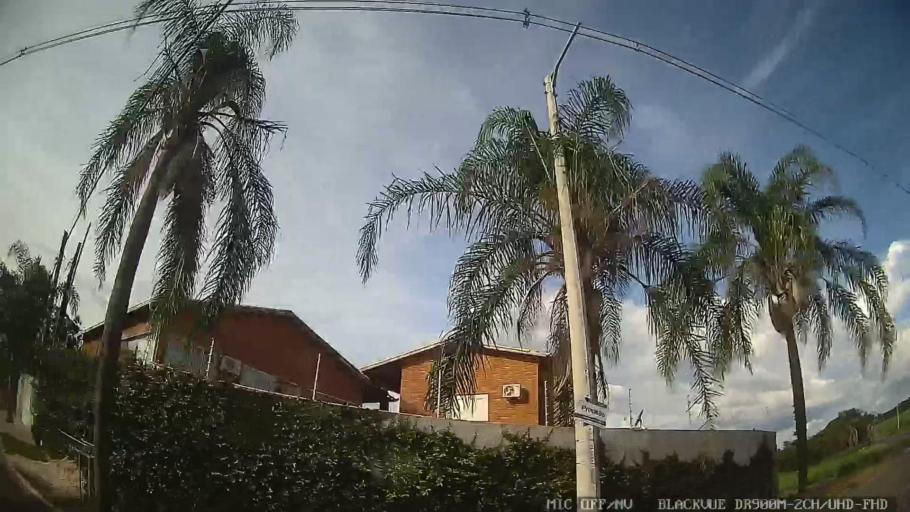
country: BR
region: Sao Paulo
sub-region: Jaguariuna
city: Jaguariuna
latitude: -22.6414
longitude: -47.0447
